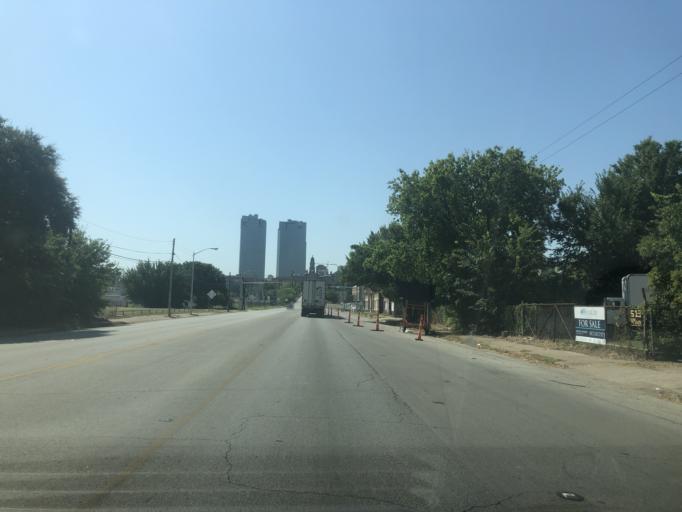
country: US
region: Texas
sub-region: Tarrant County
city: Fort Worth
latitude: 32.7648
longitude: -97.3382
